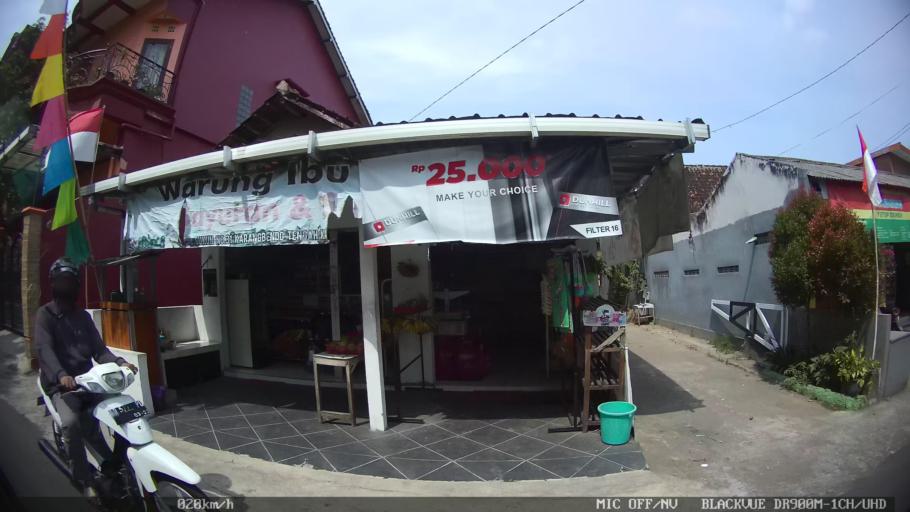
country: ID
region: Daerah Istimewa Yogyakarta
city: Depok
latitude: -7.7883
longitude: 110.4053
